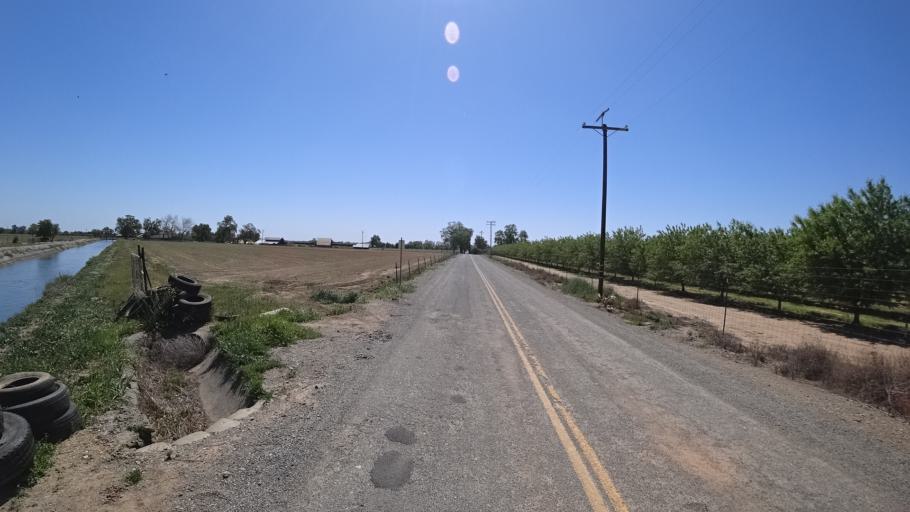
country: US
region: California
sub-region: Glenn County
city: Orland
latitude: 39.7938
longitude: -122.2300
